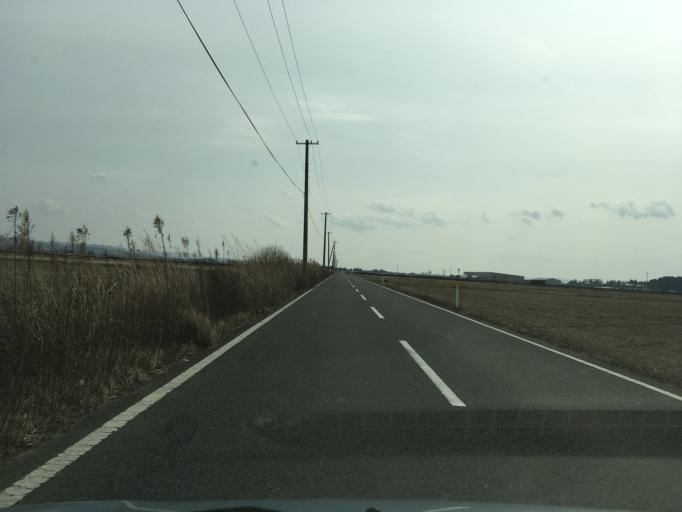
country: JP
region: Iwate
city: Ichinoseki
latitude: 38.7426
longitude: 141.2379
